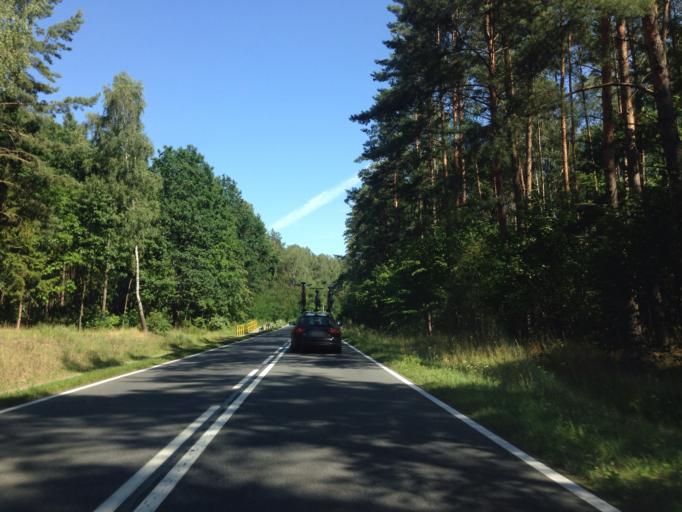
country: PL
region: Kujawsko-Pomorskie
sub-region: Powiat swiecki
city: Osie
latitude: 53.6061
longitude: 18.3245
